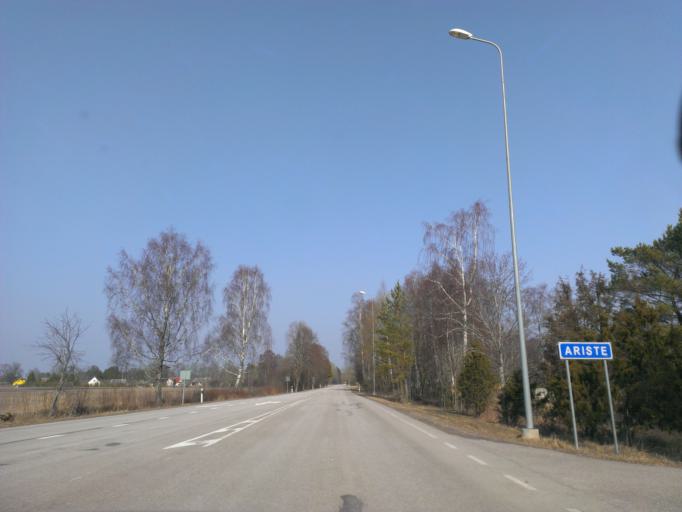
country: EE
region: Saare
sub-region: Orissaare vald
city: Orissaare
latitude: 58.5271
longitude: 23.0372
